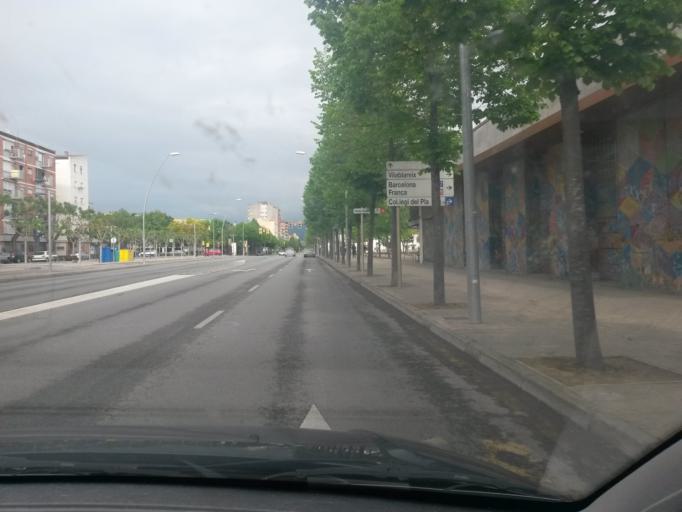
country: ES
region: Catalonia
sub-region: Provincia de Girona
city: Salt
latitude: 41.9714
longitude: 2.7850
